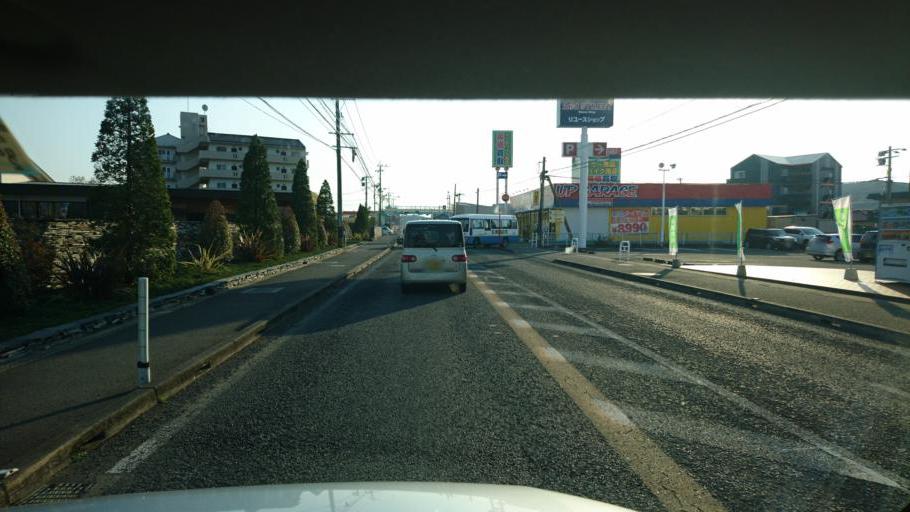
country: JP
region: Miyazaki
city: Miyazaki-shi
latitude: 31.9837
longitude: 131.4485
